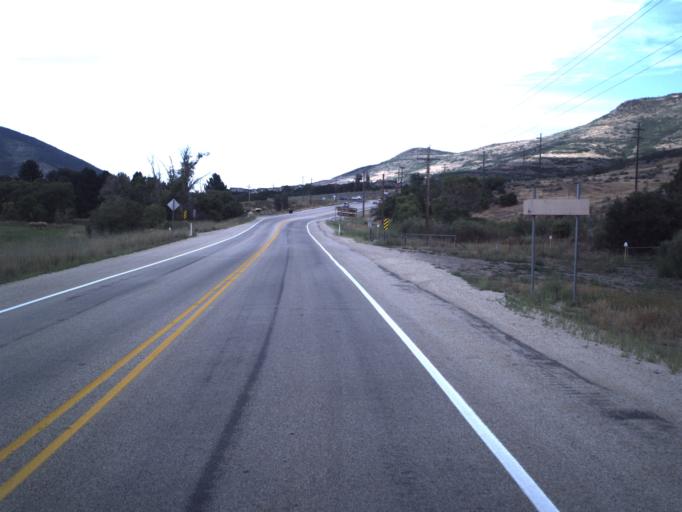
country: US
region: Utah
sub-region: Wasatch County
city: Heber
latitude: 40.5590
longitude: -111.4246
